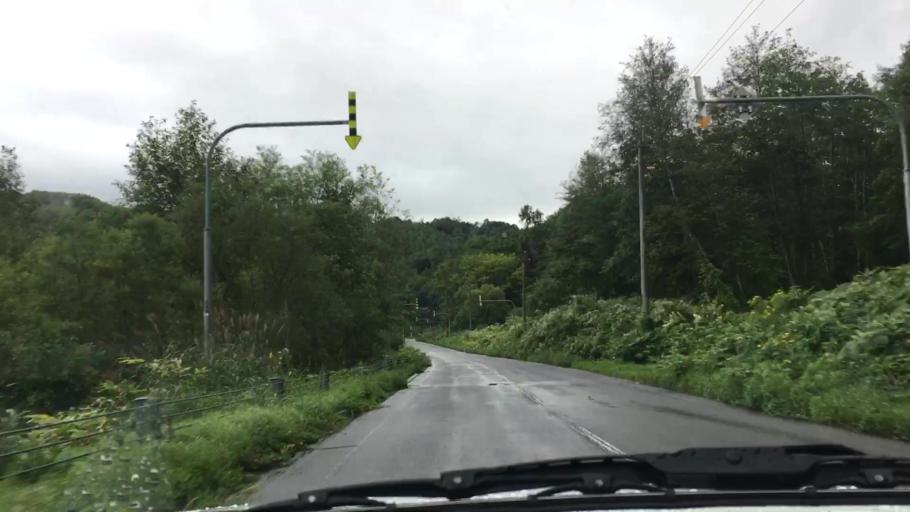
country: JP
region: Hokkaido
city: Niseko Town
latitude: 42.6659
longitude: 140.7776
